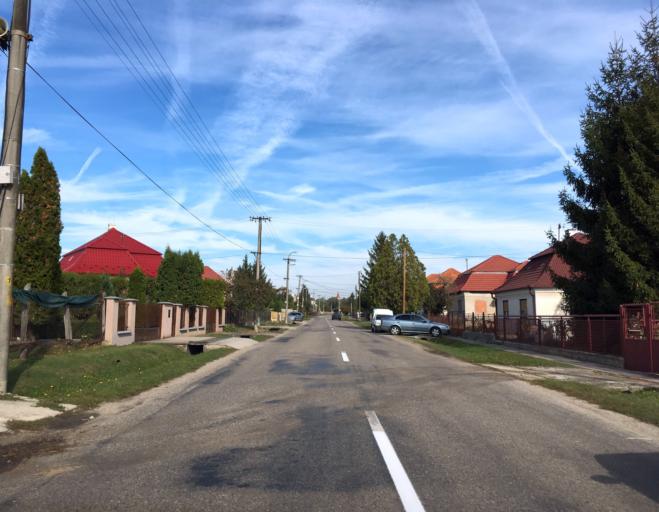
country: SK
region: Nitriansky
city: Svodin
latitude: 48.0097
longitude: 18.4140
